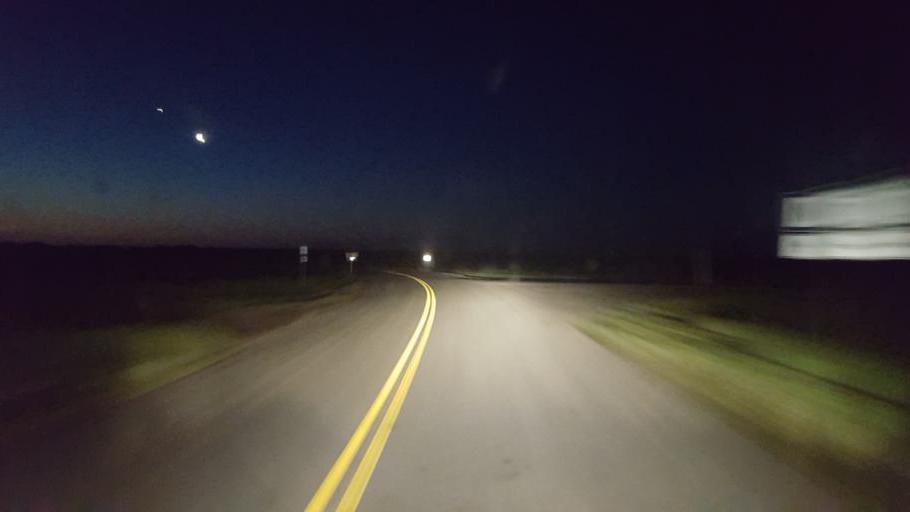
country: US
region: Iowa
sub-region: Decatur County
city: Lamoni
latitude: 40.4352
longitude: -93.8124
